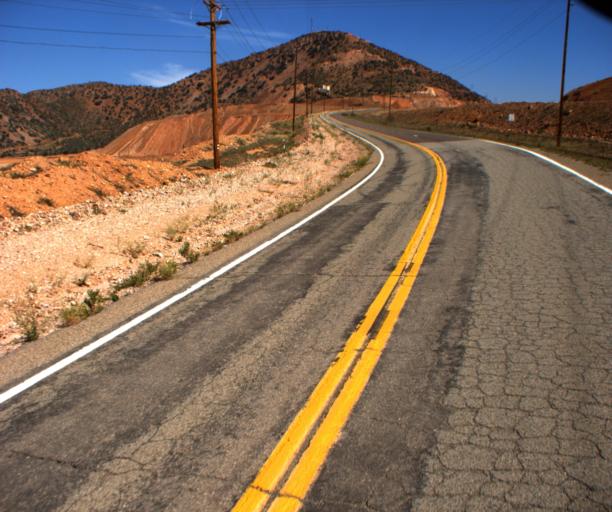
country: US
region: Arizona
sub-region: Greenlee County
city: Morenci
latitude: 33.0797
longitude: -109.3794
